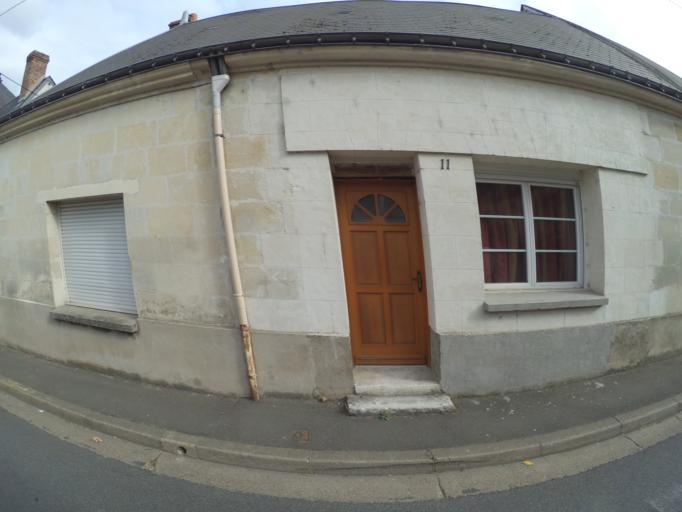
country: FR
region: Centre
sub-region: Departement d'Indre-et-Loire
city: Reugny
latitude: 47.4813
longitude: 0.8839
